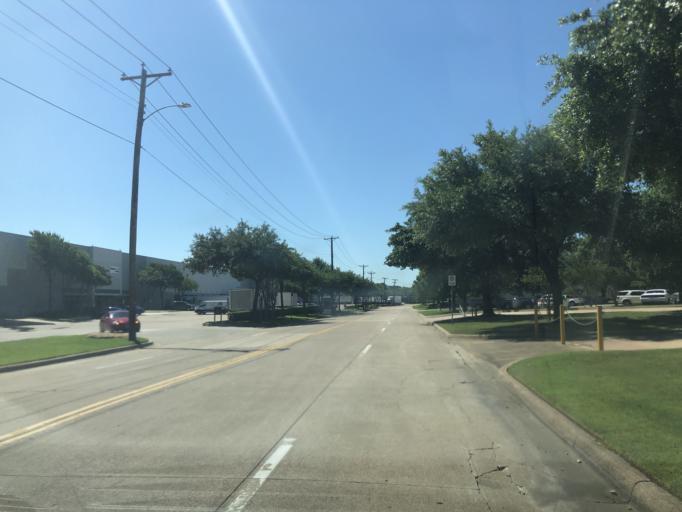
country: US
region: Texas
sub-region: Tarrant County
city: Euless
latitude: 32.7990
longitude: -97.0417
